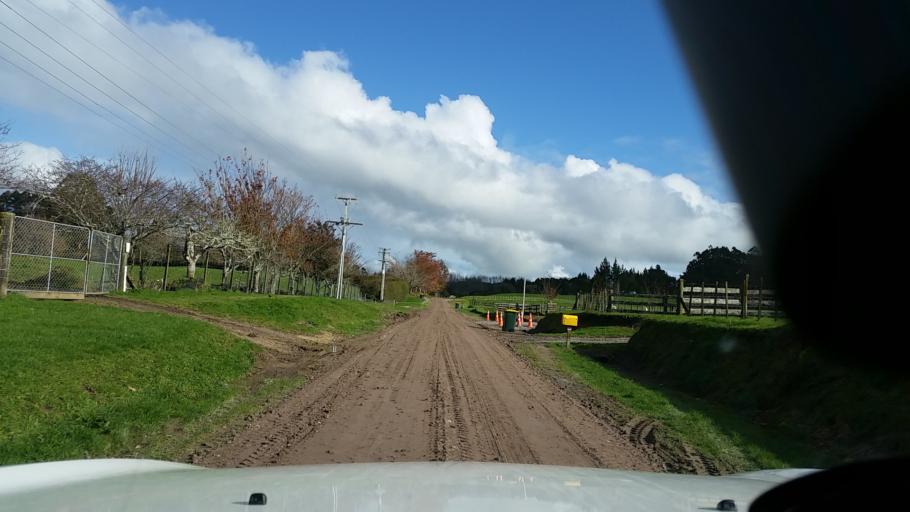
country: NZ
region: Bay of Plenty
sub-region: Rotorua District
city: Rotorua
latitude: -38.0372
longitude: 176.1952
